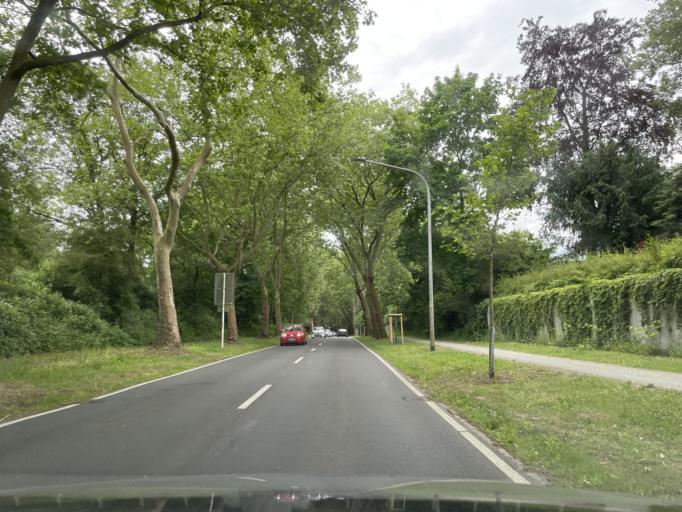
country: DE
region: North Rhine-Westphalia
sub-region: Regierungsbezirk Dusseldorf
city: Monchengladbach
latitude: 51.1540
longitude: 6.4256
